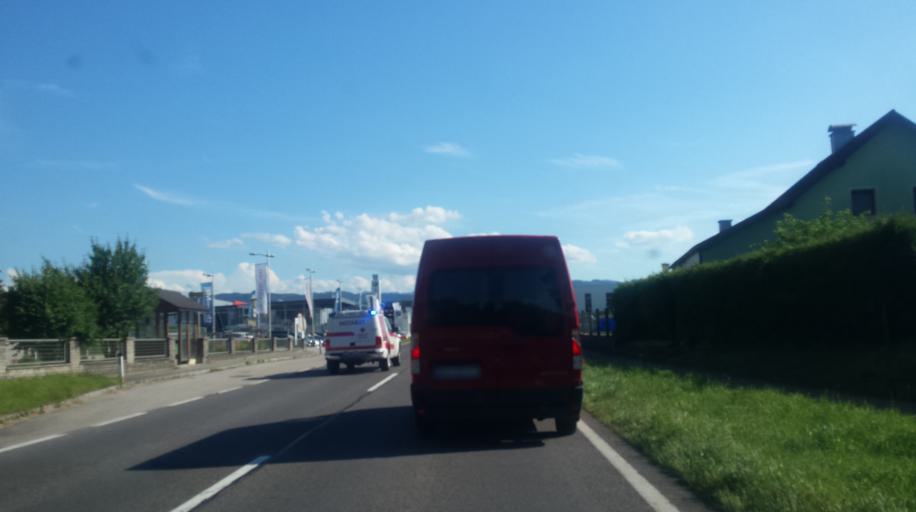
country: AT
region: Upper Austria
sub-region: Politischer Bezirk Vocklabruck
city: Attnang-Puchheim
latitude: 47.9982
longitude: 13.6843
